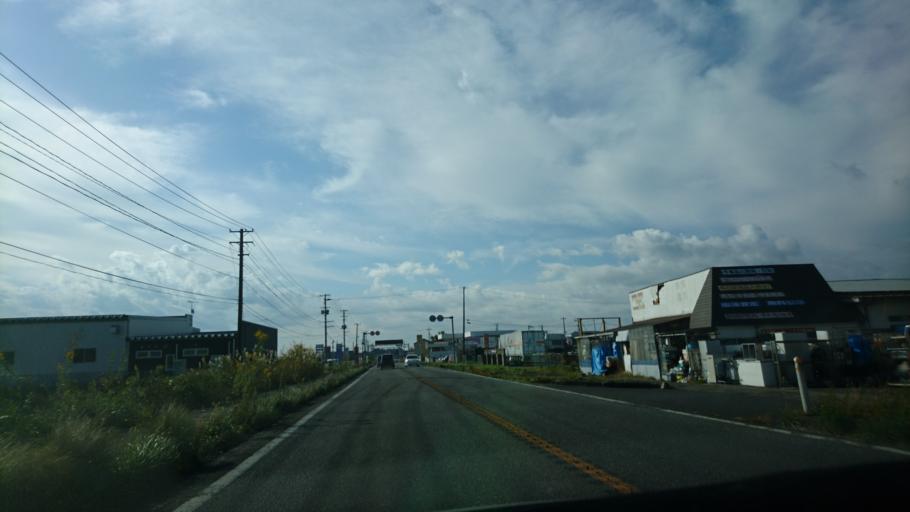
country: JP
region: Miyagi
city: Furukawa
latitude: 38.6146
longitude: 140.9836
